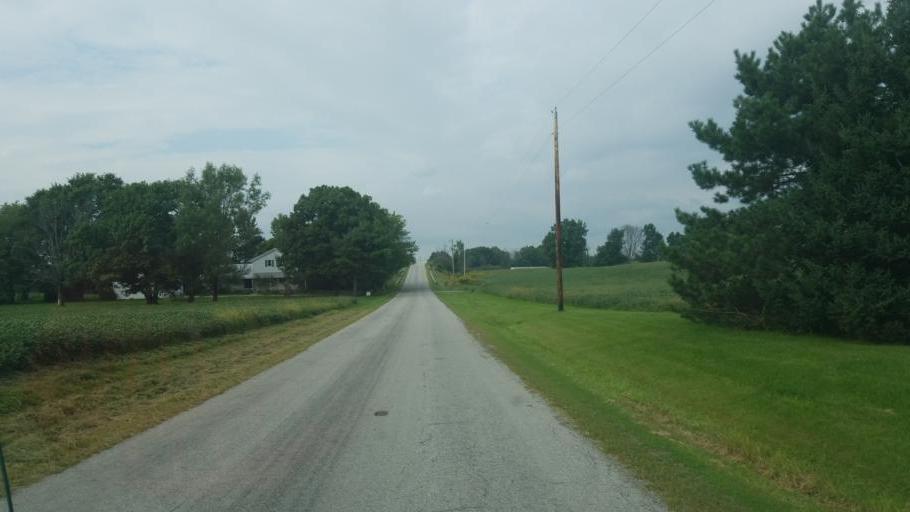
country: US
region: Ohio
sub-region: Wayne County
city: West Salem
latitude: 40.9644
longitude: -82.0538
